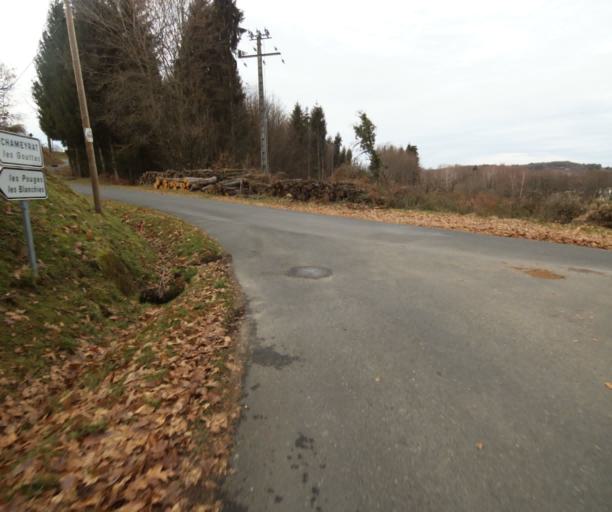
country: FR
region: Limousin
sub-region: Departement de la Correze
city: Chameyrat
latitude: 45.2417
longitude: 1.6712
